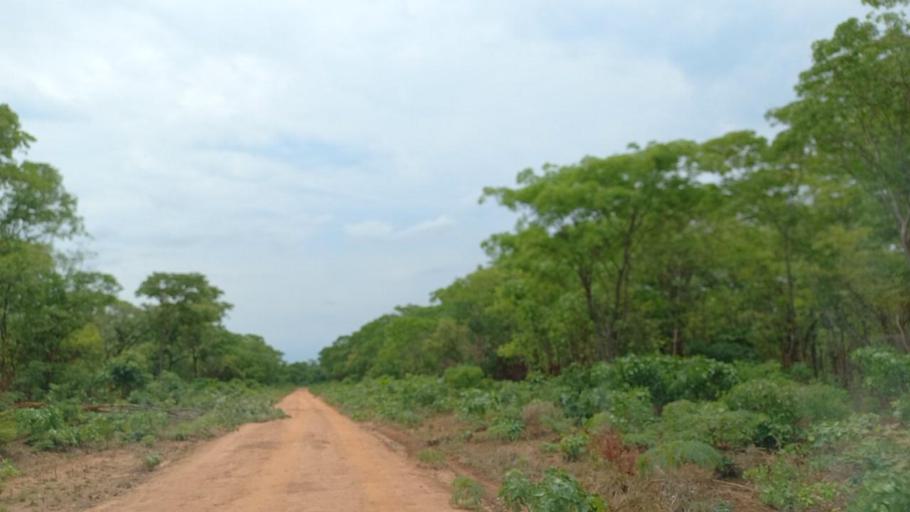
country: ZM
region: North-Western
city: Kalengwa
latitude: -13.6276
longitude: 24.9780
